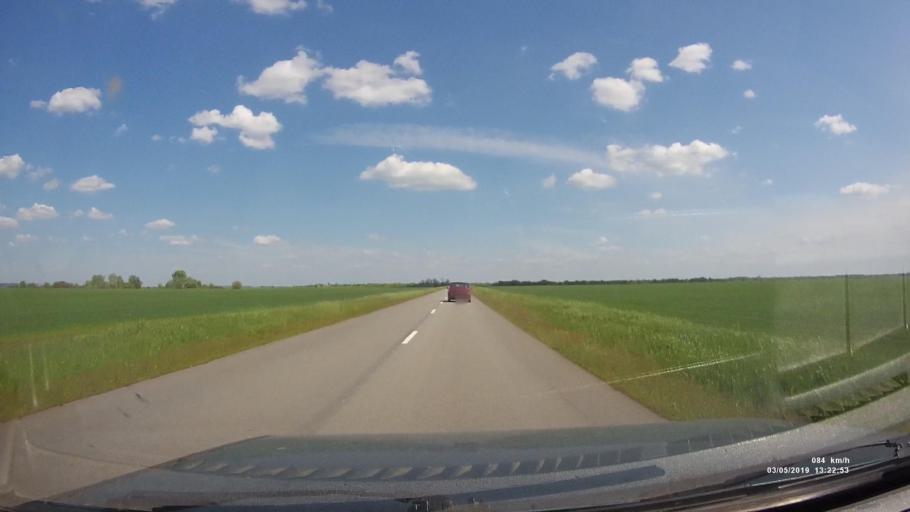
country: RU
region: Rostov
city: Semikarakorsk
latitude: 47.5625
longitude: 40.7724
